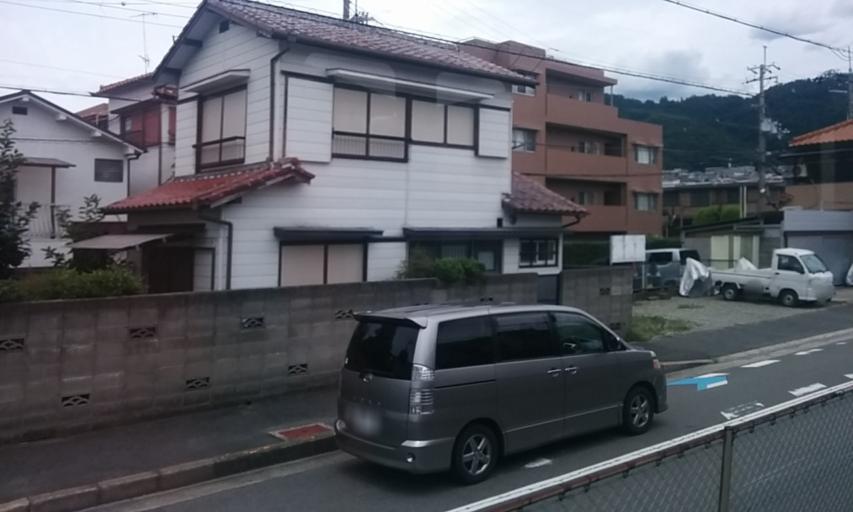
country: JP
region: Osaka
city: Mino
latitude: 34.8285
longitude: 135.4668
